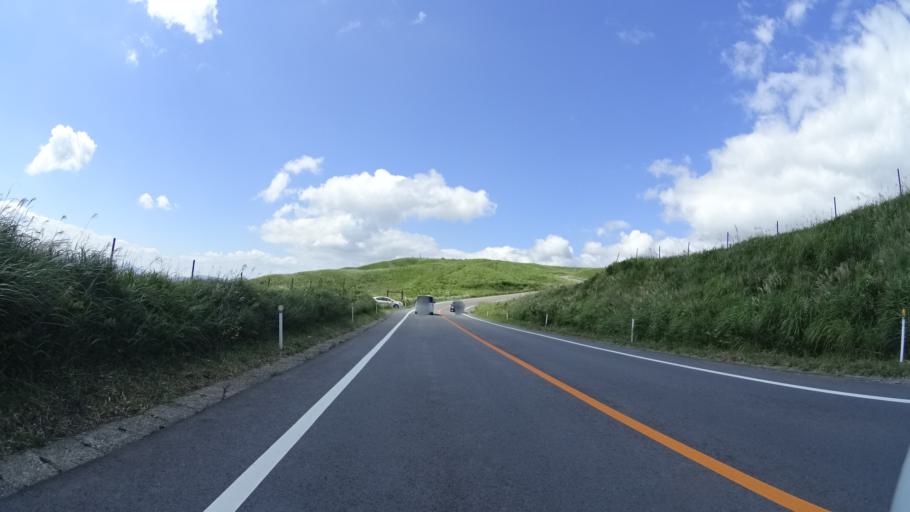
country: JP
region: Kumamoto
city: Aso
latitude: 33.0003
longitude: 131.0787
